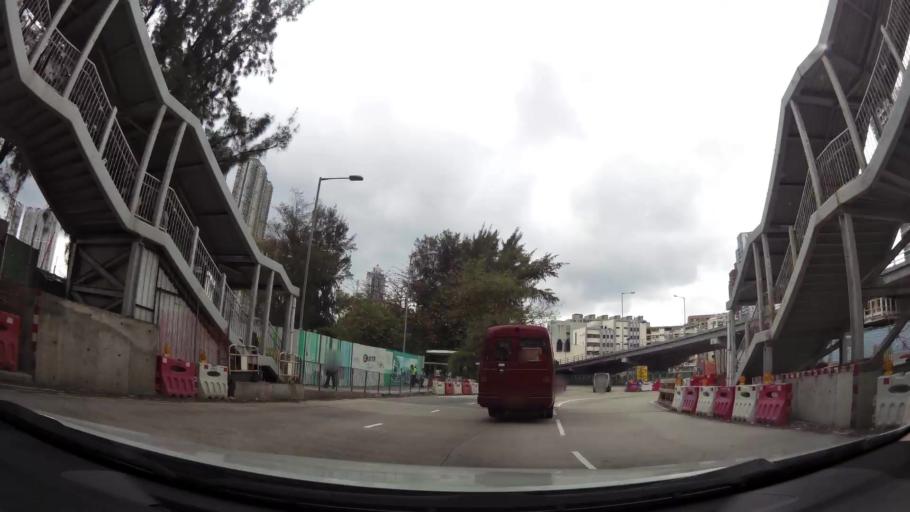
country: HK
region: Kowloon City
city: Kowloon
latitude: 22.3267
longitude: 114.1903
